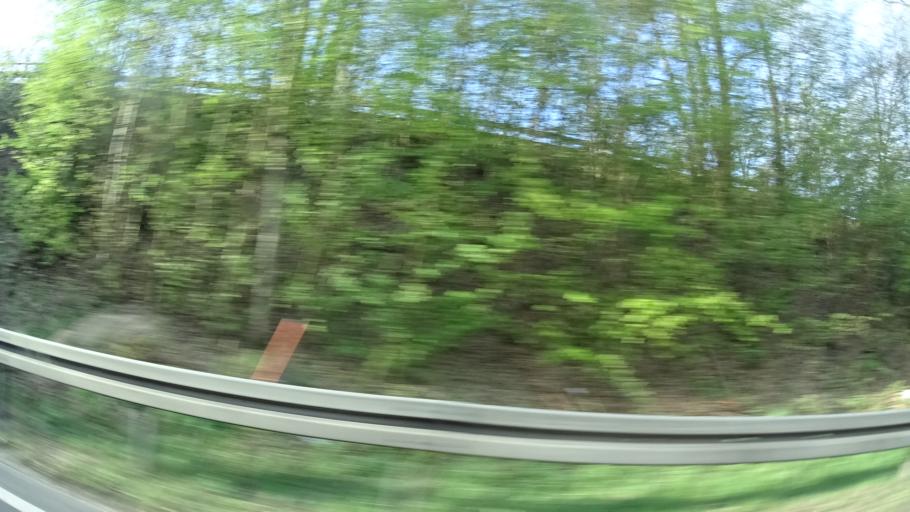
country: DE
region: Hesse
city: Viernheim
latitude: 49.5562
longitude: 8.5535
